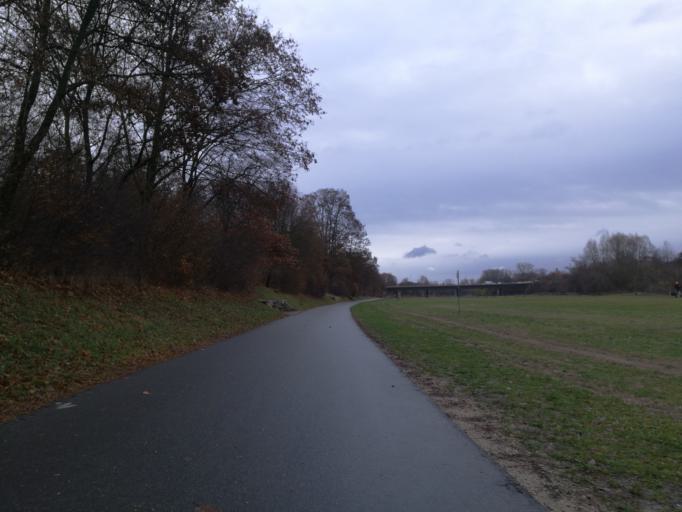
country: DE
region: Bavaria
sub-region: Regierungsbezirk Mittelfranken
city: Wetzendorf
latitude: 49.4620
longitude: 11.0416
